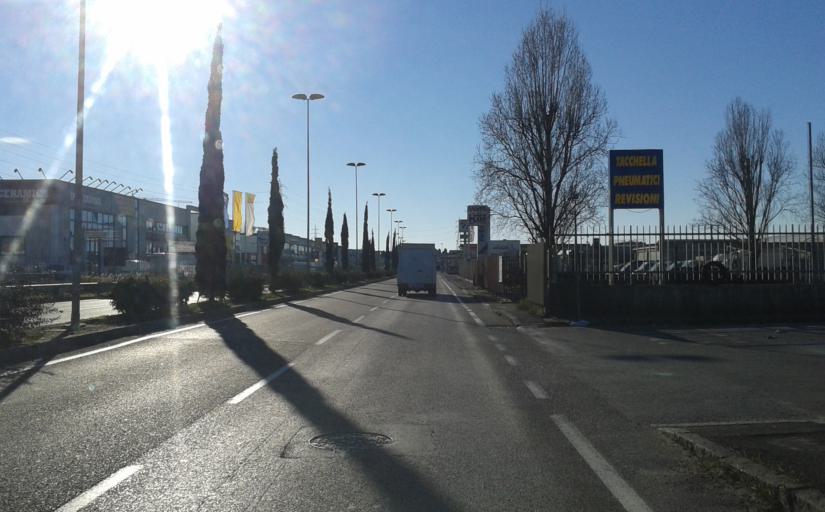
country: IT
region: Tuscany
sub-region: Provincia di Livorno
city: Livorno
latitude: 43.5765
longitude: 10.3376
